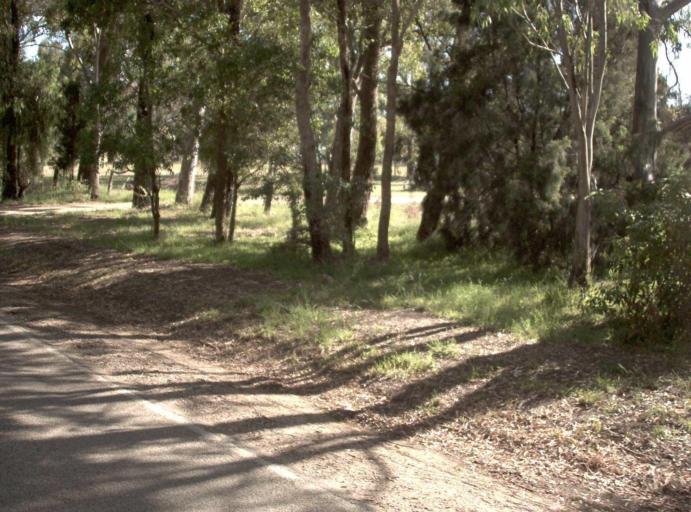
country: AU
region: Victoria
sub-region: East Gippsland
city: Lakes Entrance
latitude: -37.7696
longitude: 147.8130
